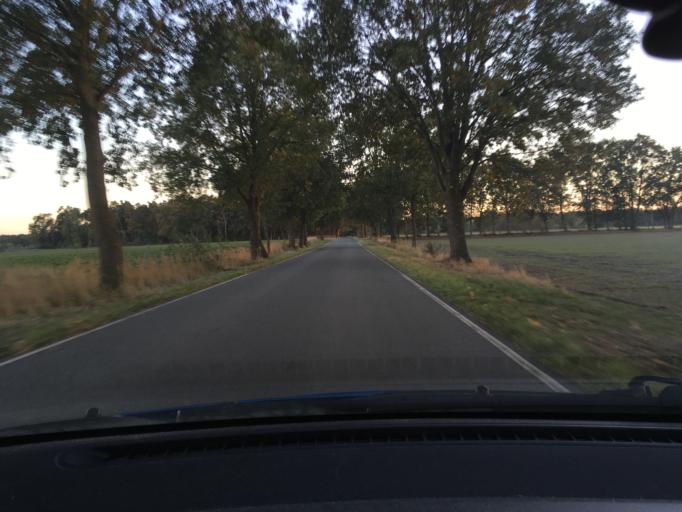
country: DE
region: Lower Saxony
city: Neetze
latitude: 53.3023
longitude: 10.6163
